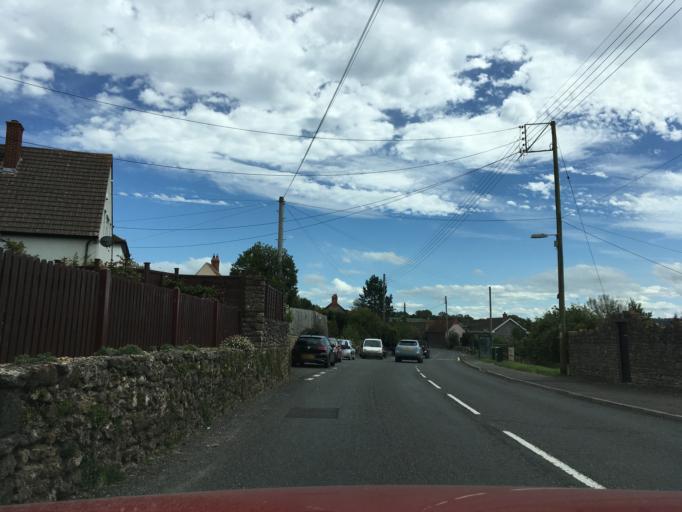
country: GB
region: England
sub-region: Somerset
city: Wells
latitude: 51.2282
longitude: -2.7022
